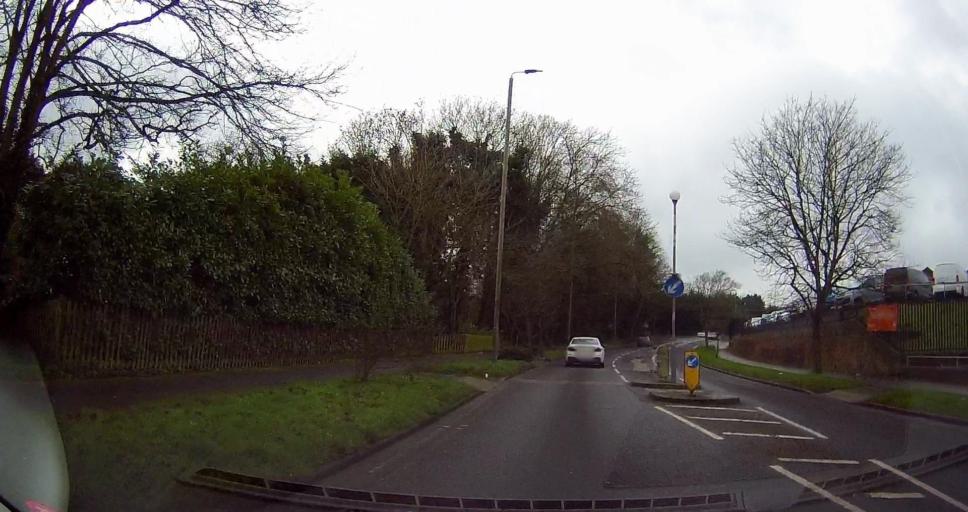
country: GB
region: England
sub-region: Greater London
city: Sidcup
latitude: 51.4175
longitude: 0.0921
